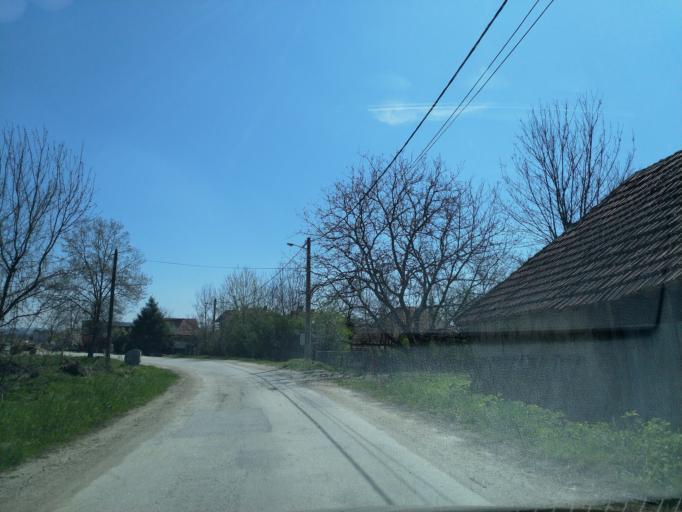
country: RS
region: Central Serbia
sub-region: Sumadijski Okrug
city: Batocina
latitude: 44.1486
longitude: 21.0671
